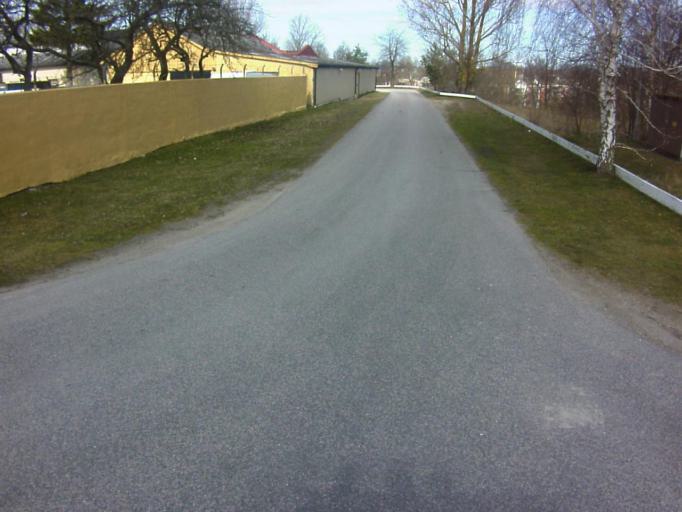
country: SE
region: Skane
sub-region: Kavlinge Kommun
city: Kaevlinge
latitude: 55.7839
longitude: 13.1137
